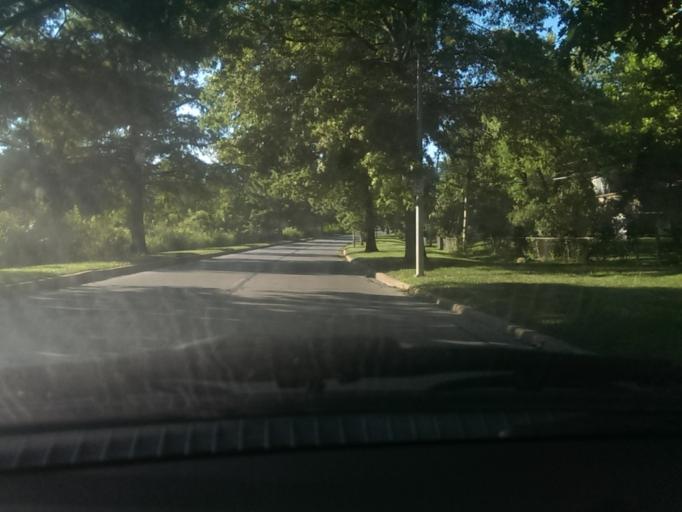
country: US
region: Kansas
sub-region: Johnson County
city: Leawood
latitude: 38.9646
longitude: -94.6046
